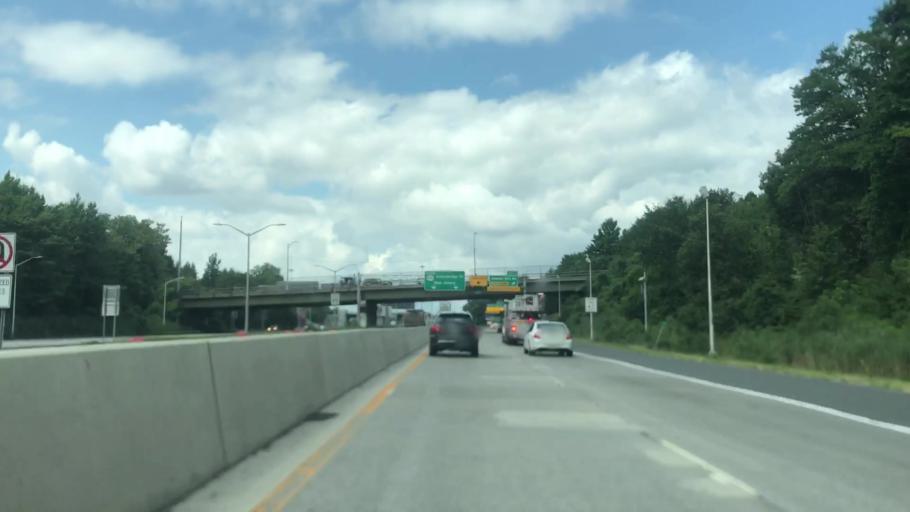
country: US
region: New Jersey
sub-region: Middlesex County
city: Sewaren
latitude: 40.5259
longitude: -74.2285
